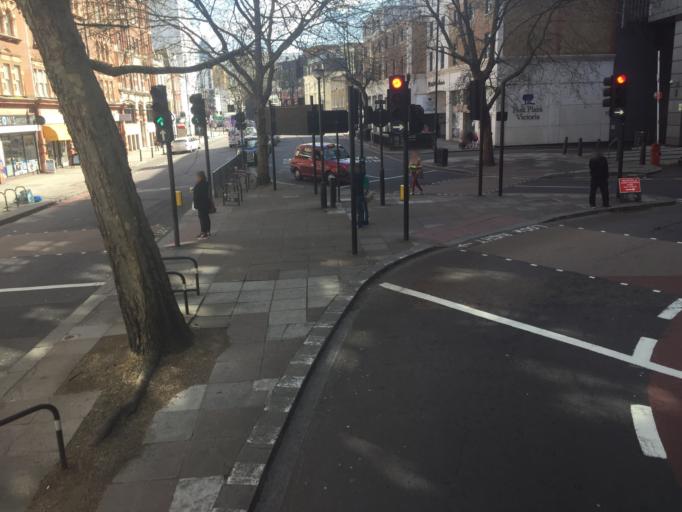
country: GB
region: England
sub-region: Greater London
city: London
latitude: 51.4950
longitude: -0.1417
